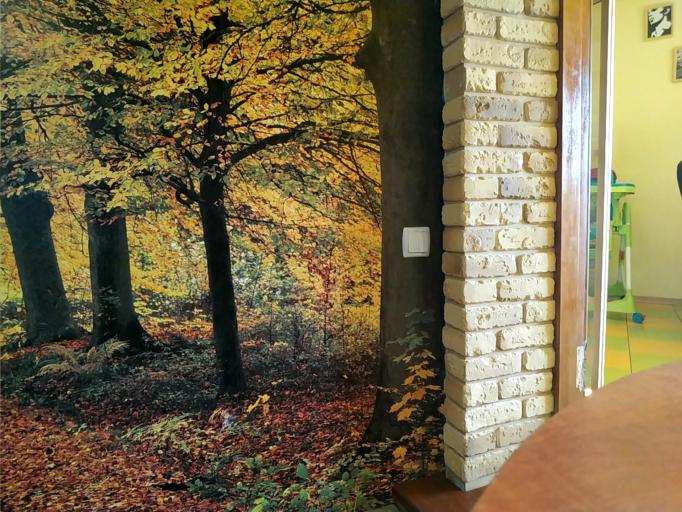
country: RU
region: Vologda
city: Nelazskoye
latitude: 59.4104
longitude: 37.6087
